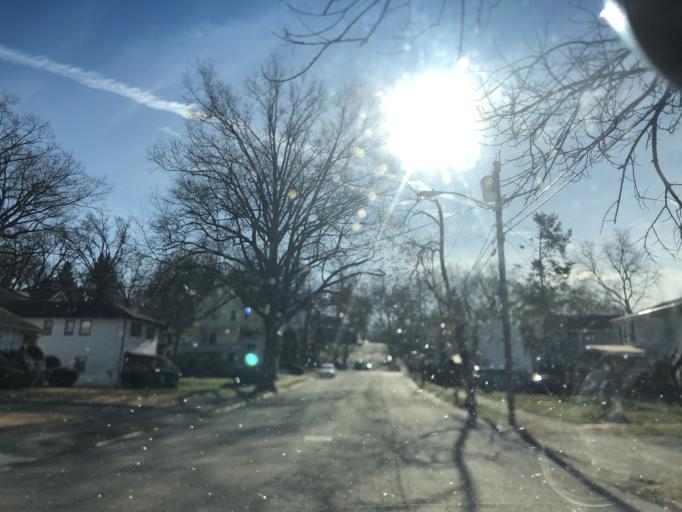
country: US
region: New Jersey
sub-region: Bergen County
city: Fair Lawn
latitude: 40.9216
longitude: -74.1374
